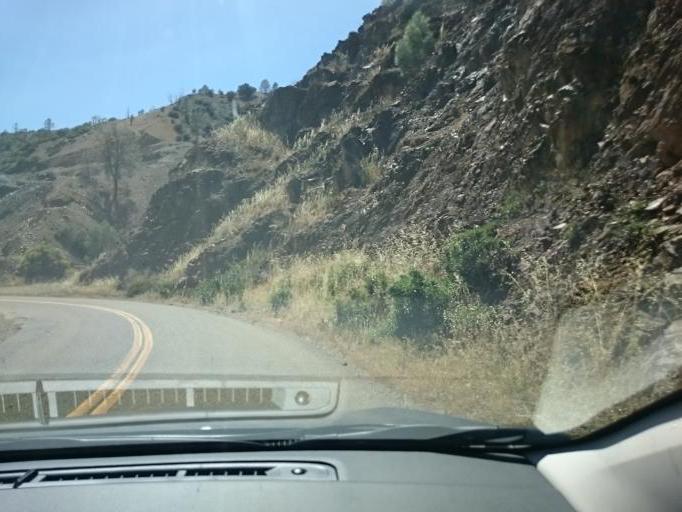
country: US
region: California
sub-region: Stanislaus County
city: Patterson
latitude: 37.4124
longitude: -121.4053
